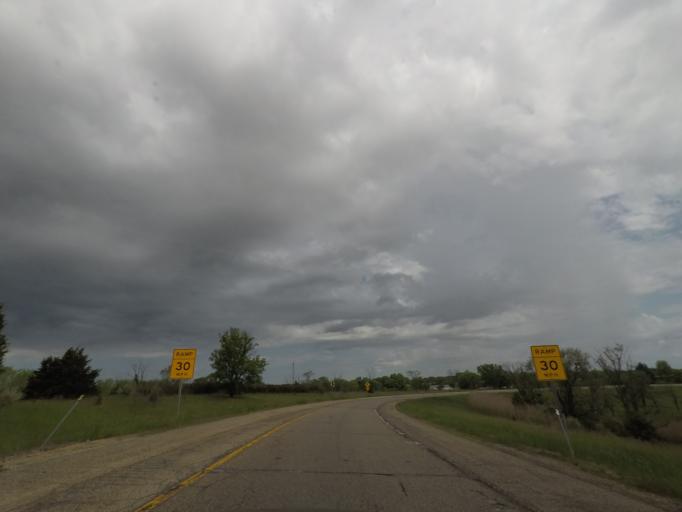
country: US
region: Illinois
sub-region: Winnebago County
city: Cherry Valley
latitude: 42.2212
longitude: -89.0110
